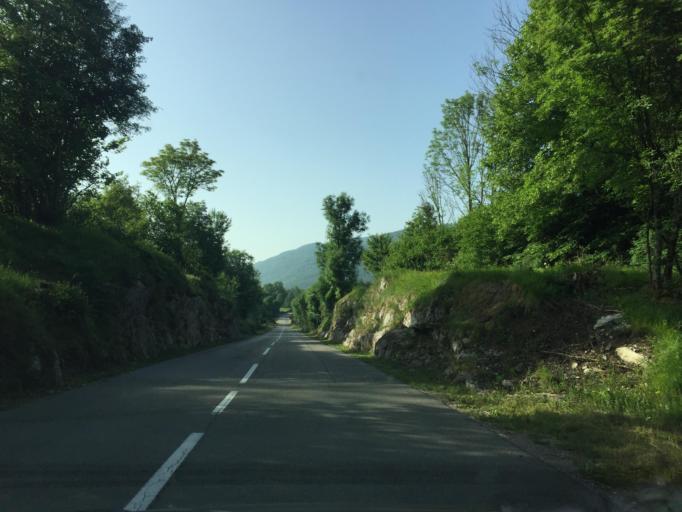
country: HR
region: Primorsko-Goranska
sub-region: Grad Opatija
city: Opatija
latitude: 45.4389
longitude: 14.1971
